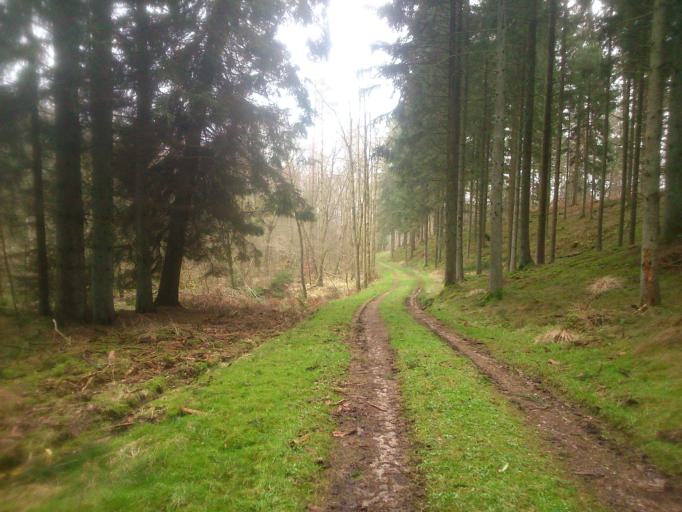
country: DK
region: Central Jutland
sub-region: Viborg Kommune
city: Bjerringbro
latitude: 56.3893
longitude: 9.7208
